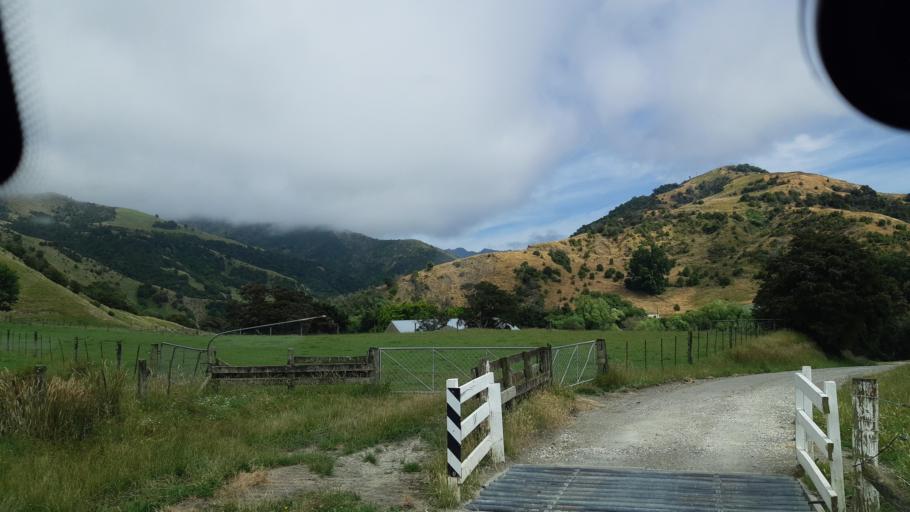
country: NZ
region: Marlborough
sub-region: Marlborough District
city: Blenheim
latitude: -41.9721
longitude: 173.9930
